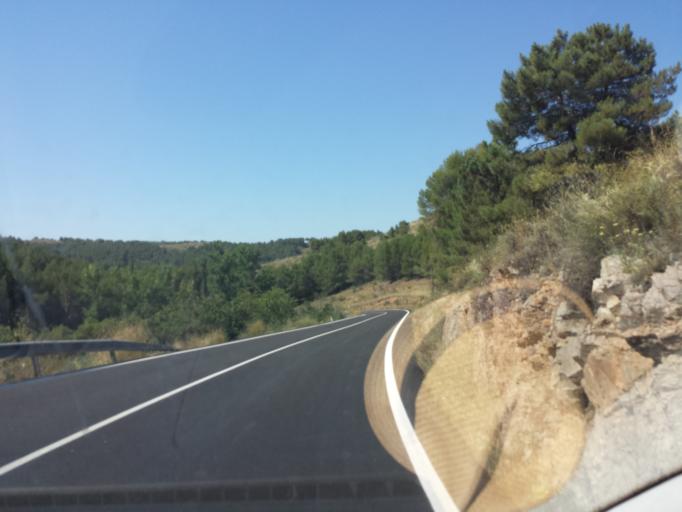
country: ES
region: Aragon
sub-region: Provincia de Zaragoza
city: Nuevalos
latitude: 41.2198
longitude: -1.7487
